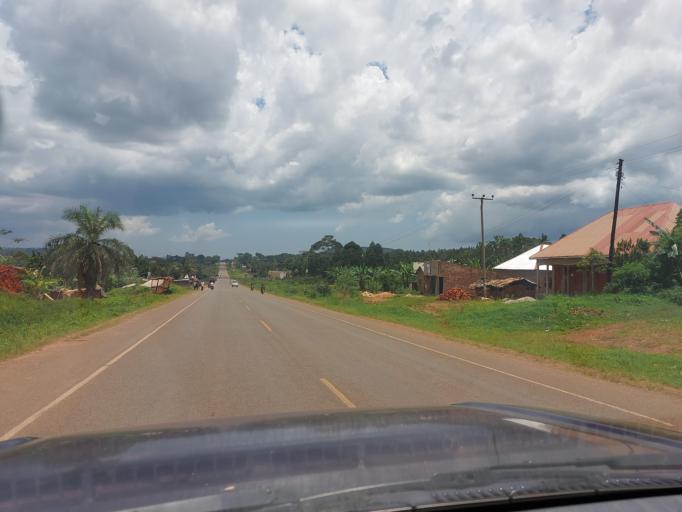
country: UG
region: Central Region
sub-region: Mukono District
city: Mukono
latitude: 0.2938
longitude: 32.7851
